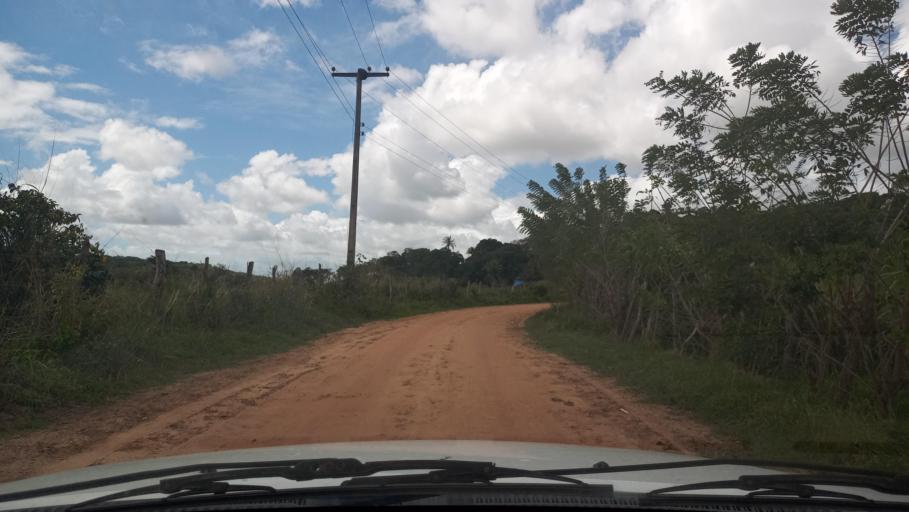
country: BR
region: Rio Grande do Norte
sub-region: Goianinha
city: Goianinha
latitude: -6.2610
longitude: -35.2537
